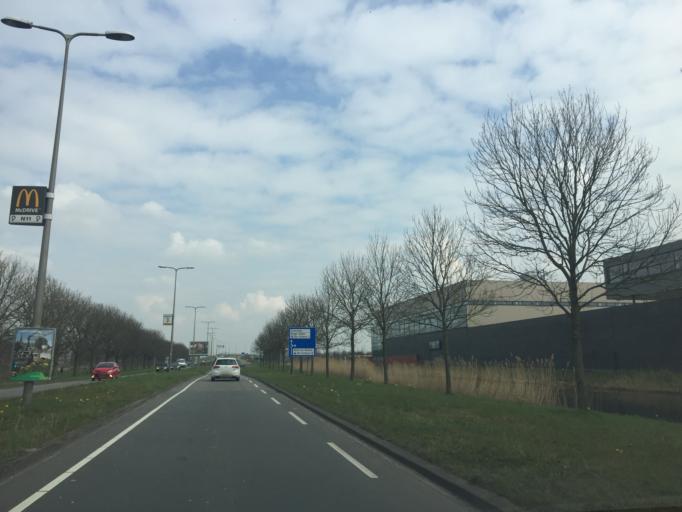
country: NL
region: South Holland
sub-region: Gemeente Alphen aan den Rijn
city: Alphen aan den Rijn
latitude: 52.1133
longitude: 4.6602
